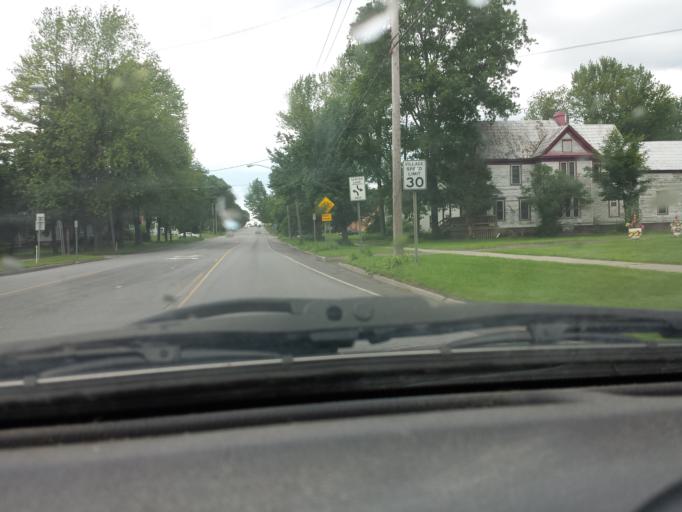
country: US
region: New York
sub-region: St. Lawrence County
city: Potsdam
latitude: 44.6730
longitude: -74.9868
